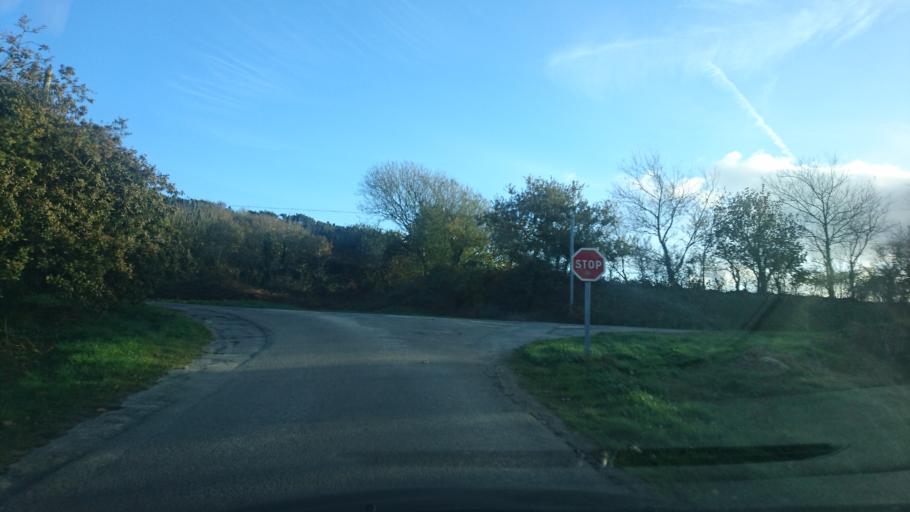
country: FR
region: Brittany
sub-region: Departement du Finistere
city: Lampaul-Plouarzel
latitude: 48.4366
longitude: -4.7589
